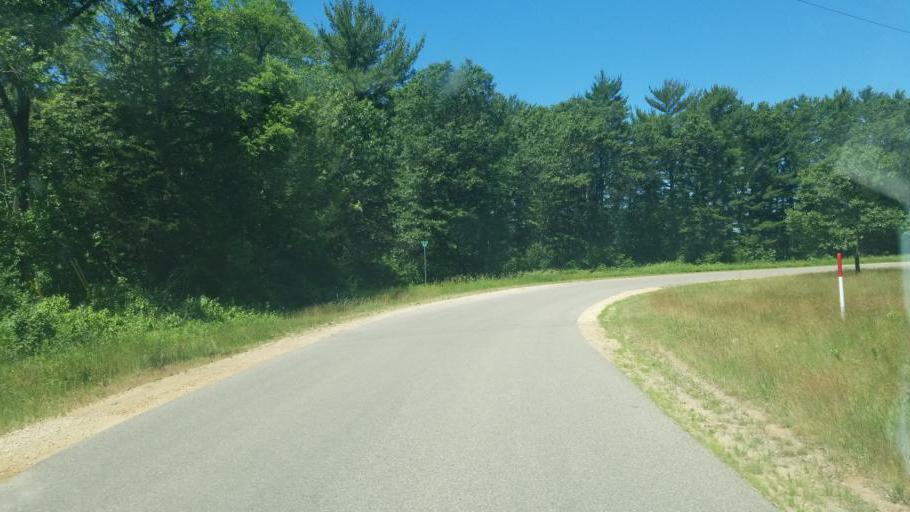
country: US
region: Wisconsin
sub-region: Adams County
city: Friendship
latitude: 43.9817
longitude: -89.9539
